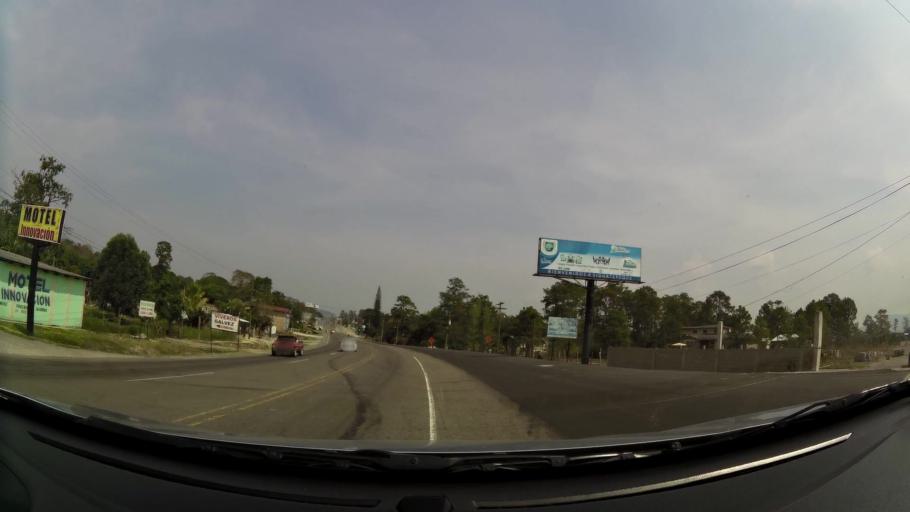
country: HN
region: Comayagua
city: Siguatepeque
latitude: 14.5751
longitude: -87.8323
